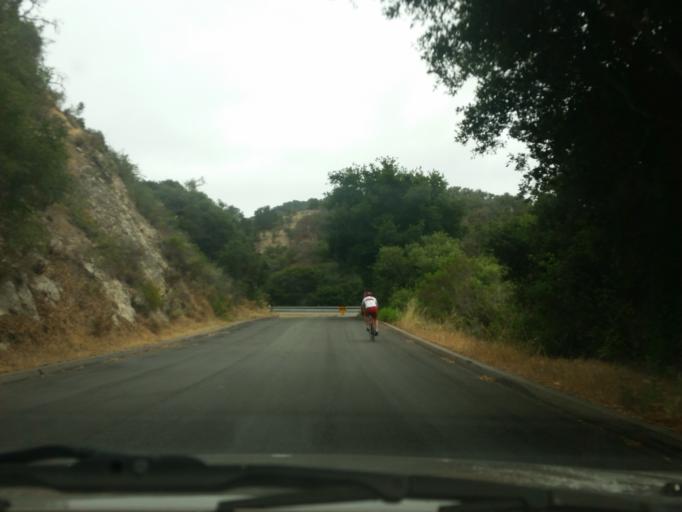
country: US
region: California
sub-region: San Luis Obispo County
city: Avila Beach
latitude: 35.1832
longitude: -120.7002
